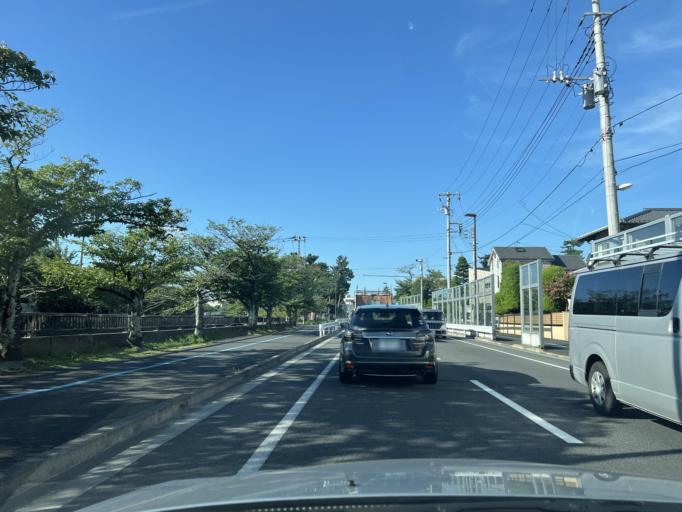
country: JP
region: Chiba
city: Funabashi
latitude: 35.7248
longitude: 139.9370
